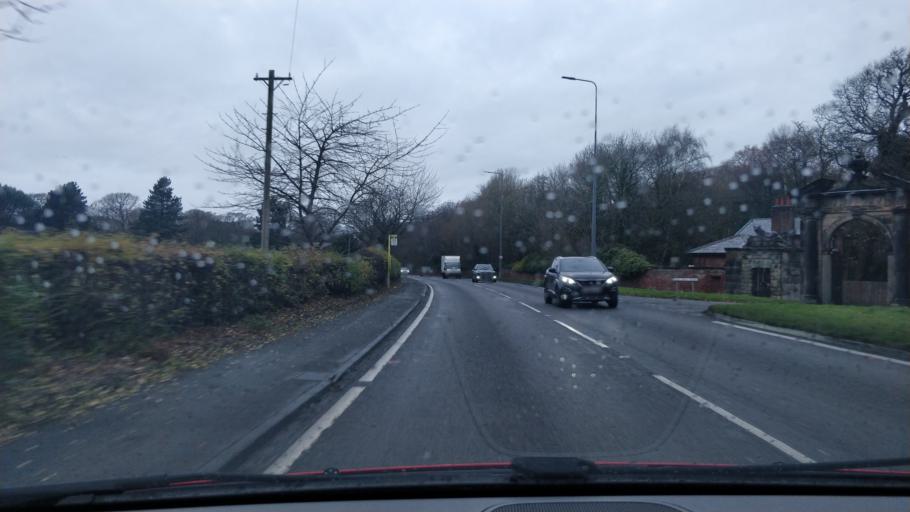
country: GB
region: England
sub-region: Sefton
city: Thornton
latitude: 53.5111
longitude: -3.0120
